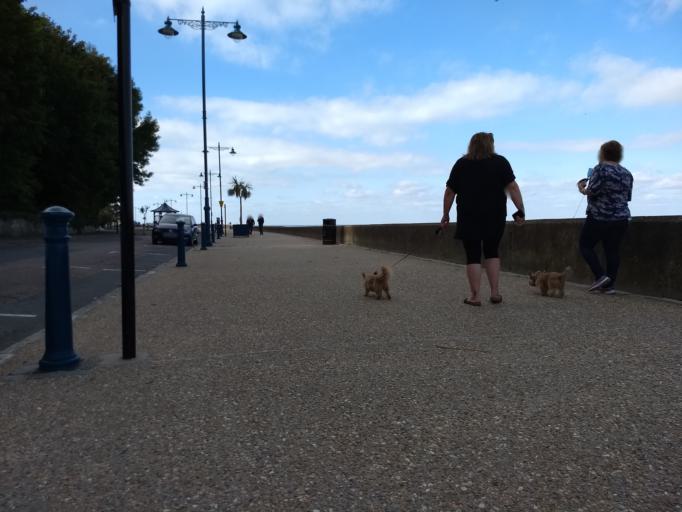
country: GB
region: England
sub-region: Isle of Wight
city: Ryde
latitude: 50.7288
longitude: -1.1442
